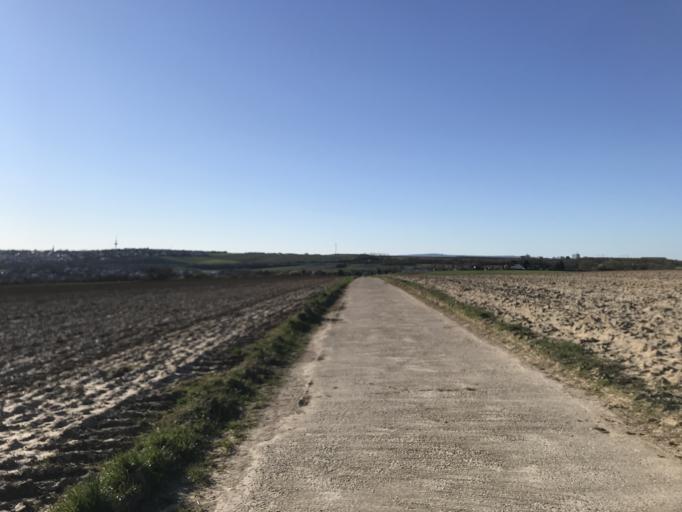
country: DE
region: Rheinland-Pfalz
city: Klein-Winternheim
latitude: 49.9372
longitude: 8.2303
